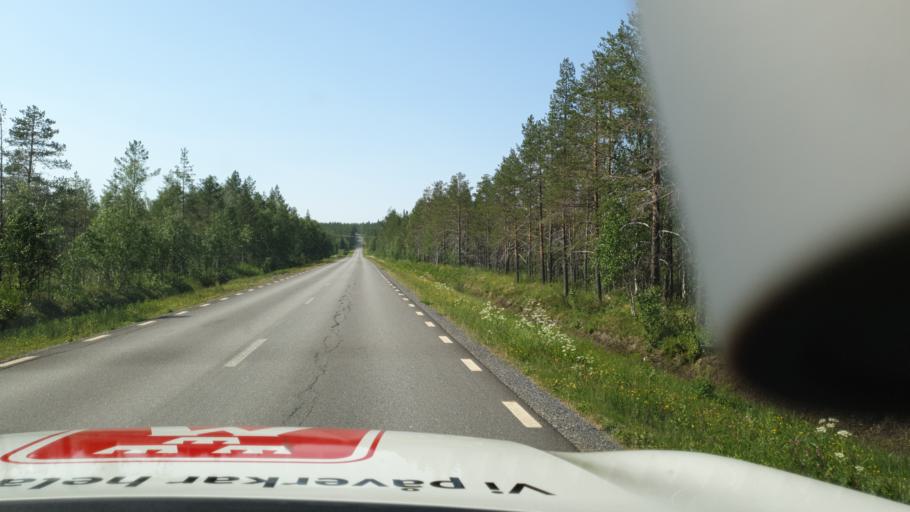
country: SE
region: Vaesterbotten
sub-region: Skelleftea Kommun
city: Langsele
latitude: 64.9828
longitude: 20.0696
